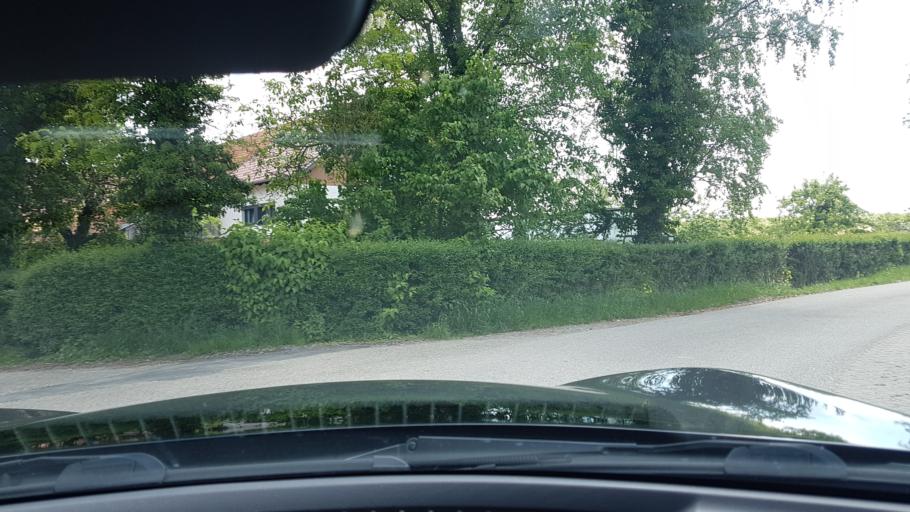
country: DE
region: Baden-Wuerttemberg
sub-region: Regierungsbezirk Stuttgart
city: Jagsthausen
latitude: 49.2634
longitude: 9.4372
